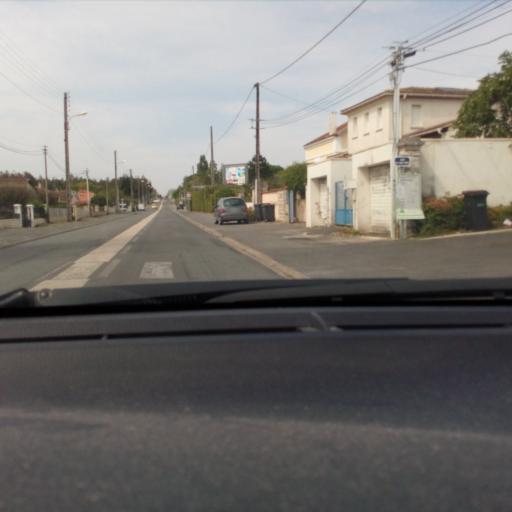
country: FR
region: Poitou-Charentes
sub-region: Departement de la Charente
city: Saint-Yrieix-sur-Charente
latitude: 45.6700
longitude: 0.1296
